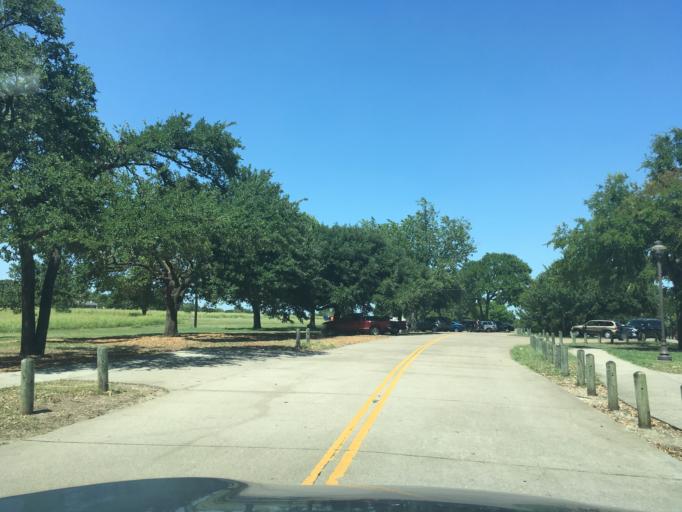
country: US
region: Texas
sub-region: Dallas County
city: Highland Park
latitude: 32.8612
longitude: -96.7254
